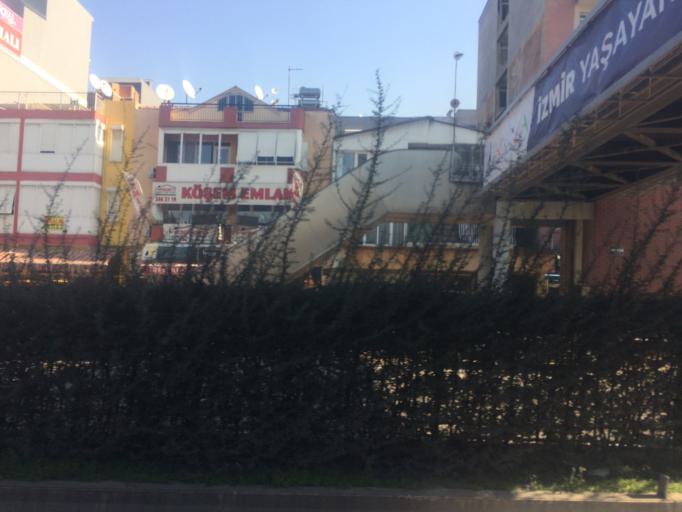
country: TR
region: Izmir
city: Karsiyaka
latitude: 38.5000
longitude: 27.0552
